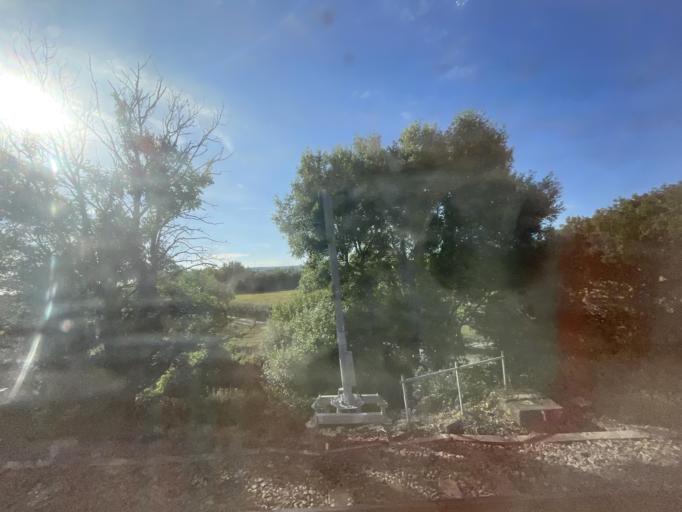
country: GB
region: Wales
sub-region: Gwynedd
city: Aber
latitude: 53.2375
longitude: -4.0258
